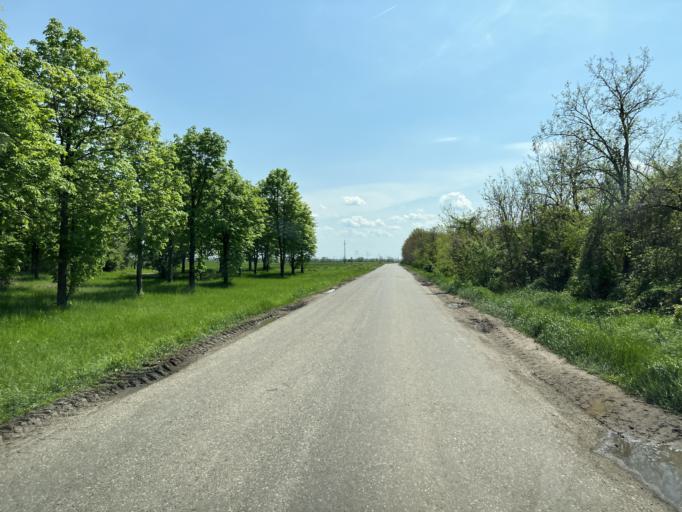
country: HU
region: Pest
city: Cegled
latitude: 47.2529
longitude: 19.7744
